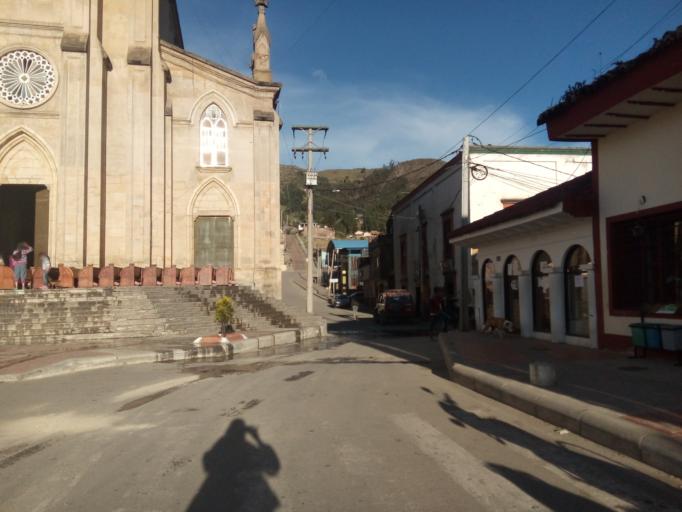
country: CO
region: Boyaca
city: Gameza
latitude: 5.8017
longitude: -72.8049
